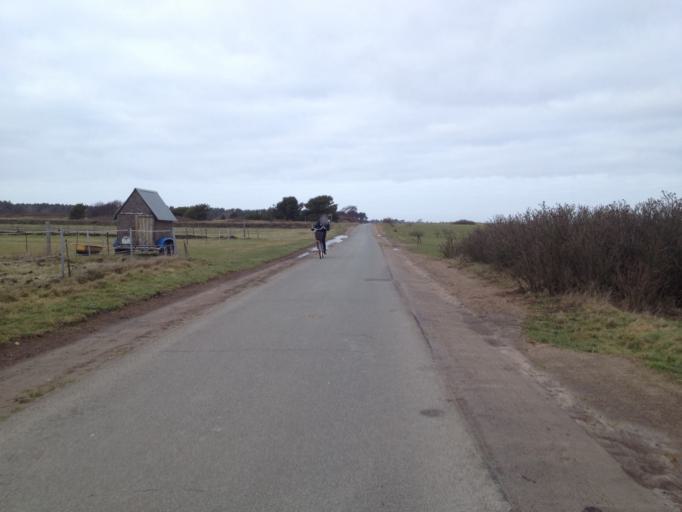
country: DE
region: Schleswig-Holstein
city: Nebel
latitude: 54.6638
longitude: 8.3463
